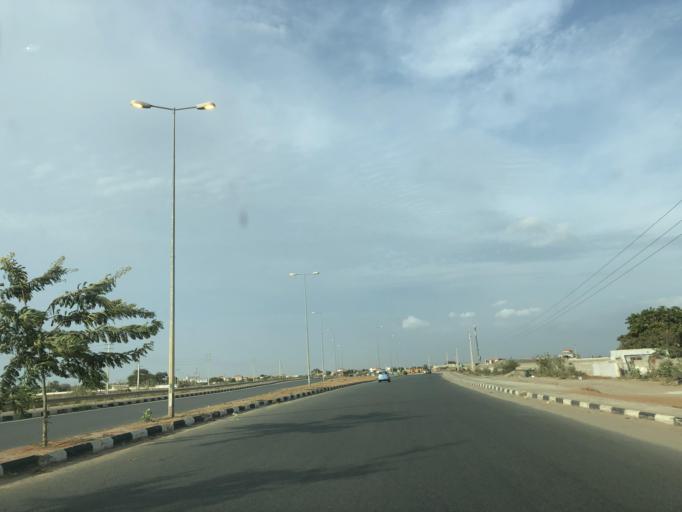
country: AO
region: Luanda
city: Luanda
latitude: -8.9355
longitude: 13.2982
